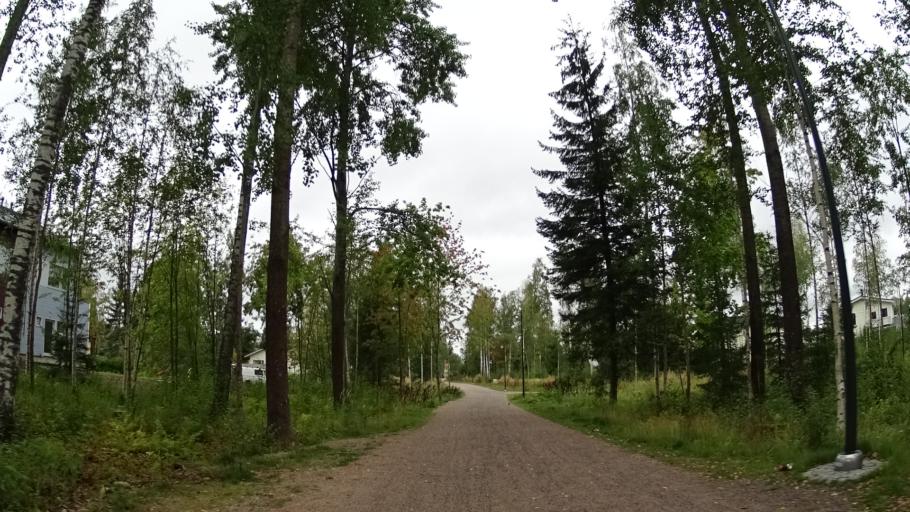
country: FI
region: Uusimaa
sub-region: Helsinki
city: Kilo
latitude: 60.3213
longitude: 24.8494
